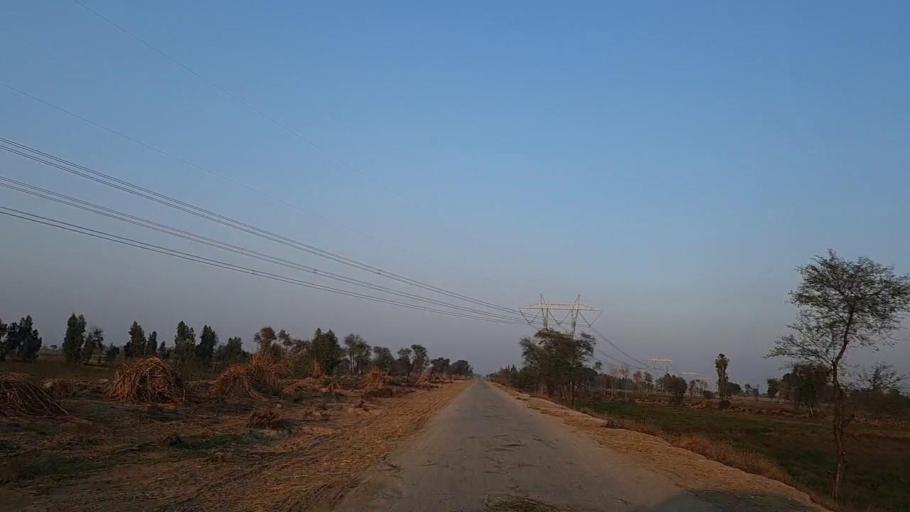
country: PK
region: Sindh
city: Naushahro Firoz
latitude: 26.7699
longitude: 68.0559
